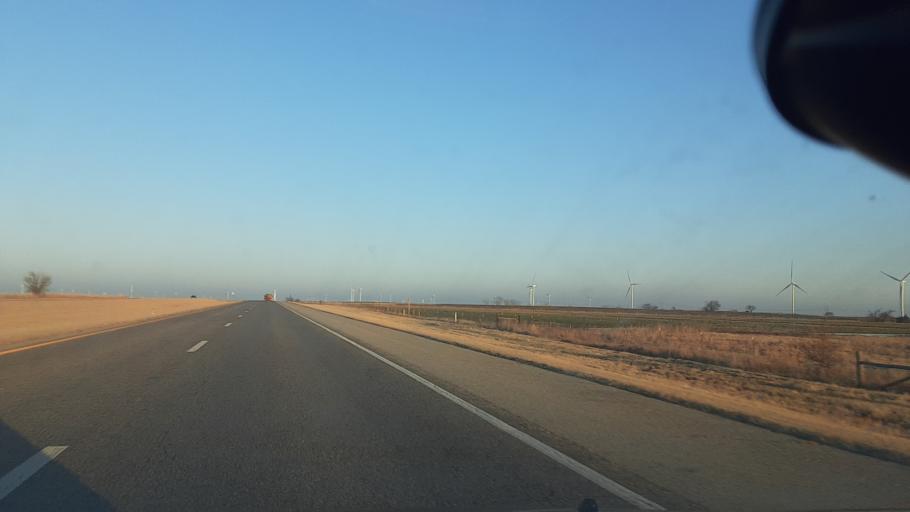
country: US
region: Oklahoma
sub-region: Noble County
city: Perry
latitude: 36.3975
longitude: -97.5002
